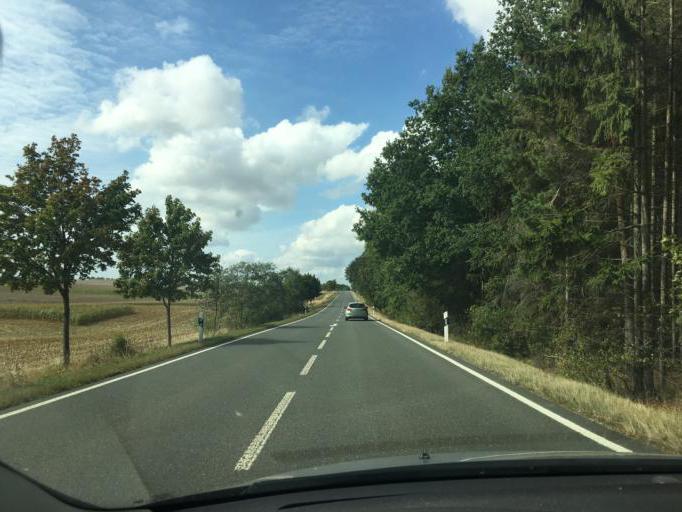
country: DE
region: Thuringia
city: Pormitz
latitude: 50.6151
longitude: 11.8336
